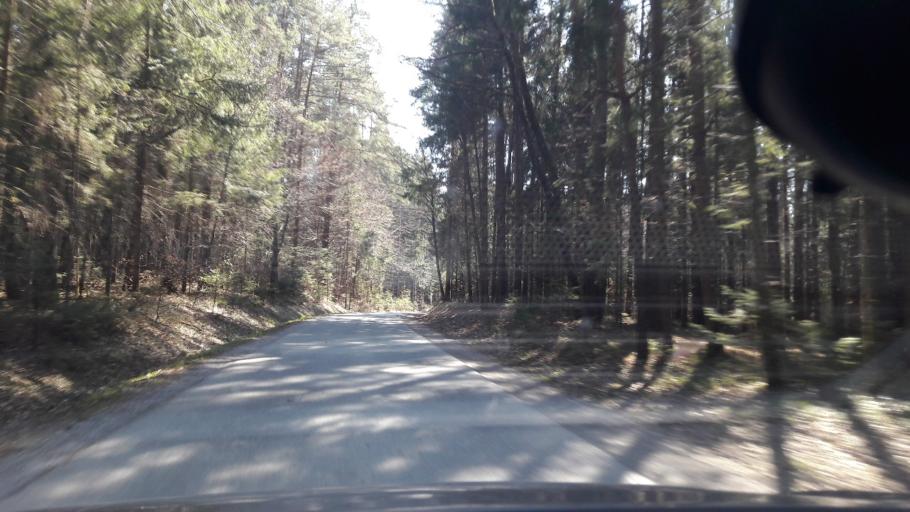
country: AT
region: Styria
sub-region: Politischer Bezirk Graz-Umgebung
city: Hitzendorf
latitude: 47.0305
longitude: 15.3118
